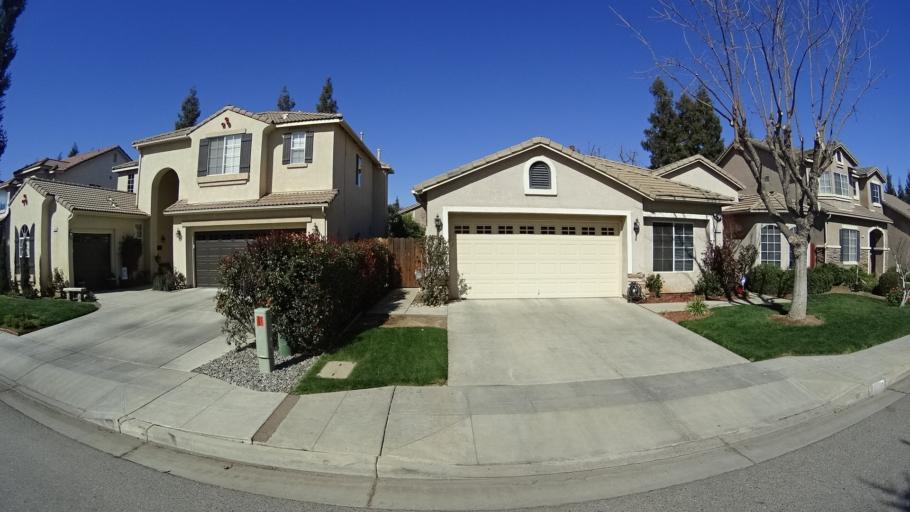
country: US
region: California
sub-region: Fresno County
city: Clovis
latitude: 36.8562
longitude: -119.7366
